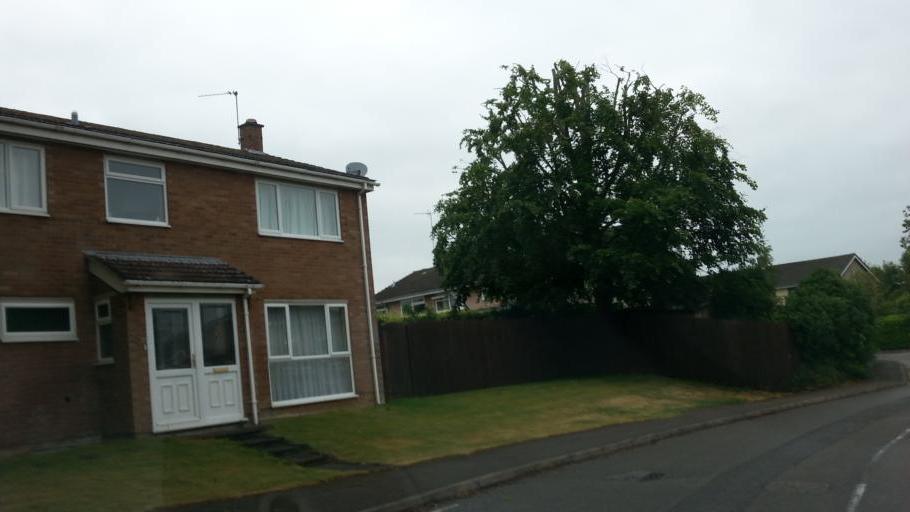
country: GB
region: England
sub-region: Cambridgeshire
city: Histon
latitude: 52.2574
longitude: 0.1031
